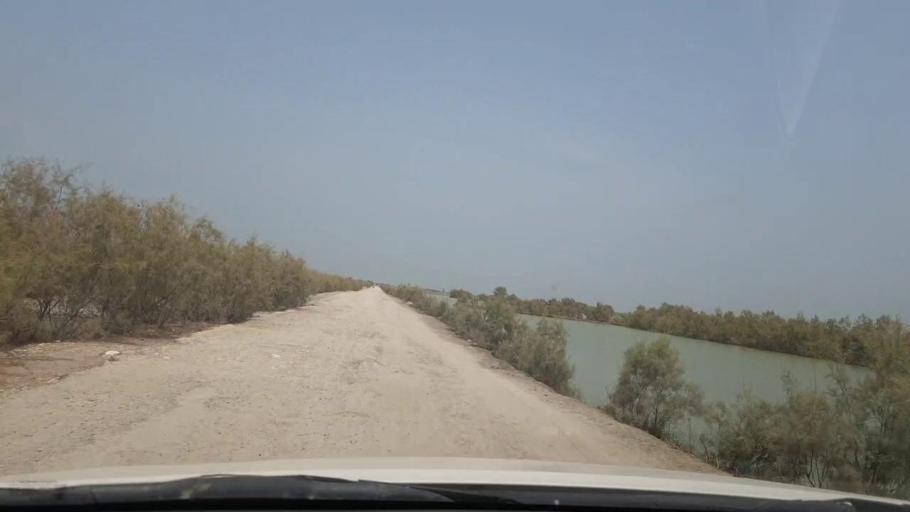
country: PK
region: Sindh
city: Rustam jo Goth
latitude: 28.0612
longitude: 68.8166
